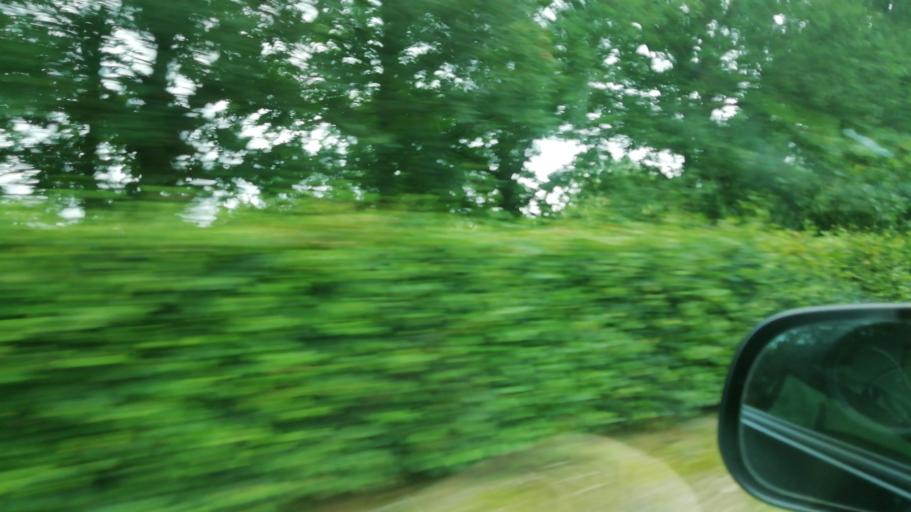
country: IE
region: Munster
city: Fethard
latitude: 52.4932
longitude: -7.6899
